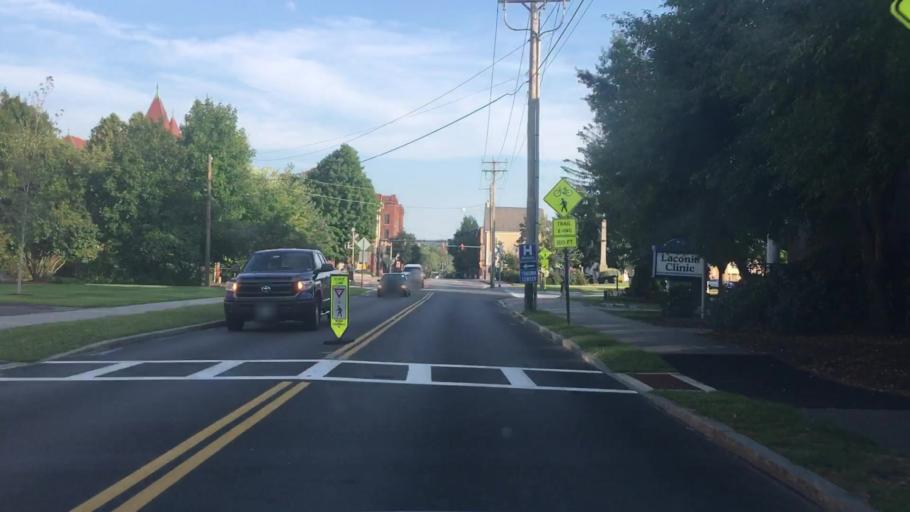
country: US
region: New Hampshire
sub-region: Belknap County
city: Laconia
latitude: 43.5306
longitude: -71.4720
